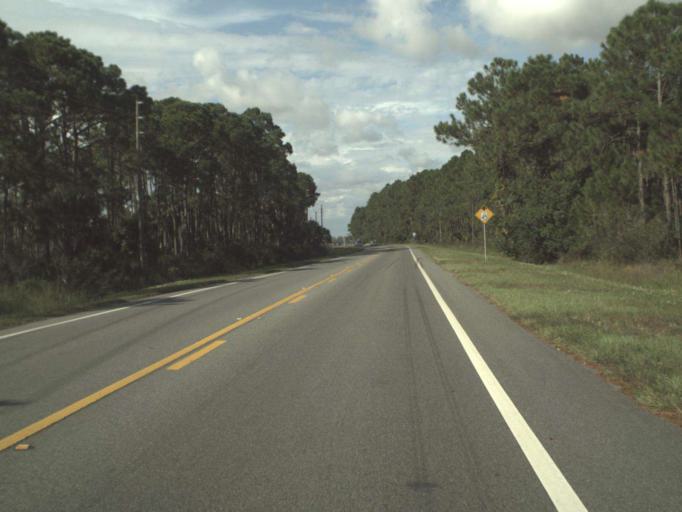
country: US
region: Florida
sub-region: Gulf County
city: Port Saint Joe
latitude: 29.7856
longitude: -85.3012
